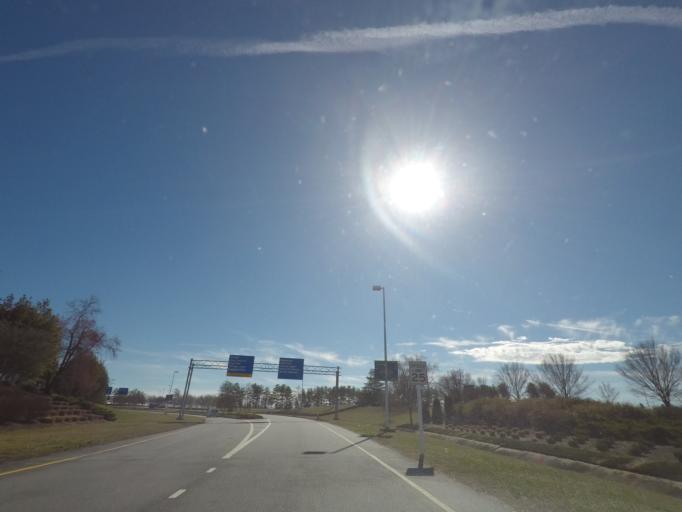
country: US
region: North Carolina
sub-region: Guilford County
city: Oak Ridge
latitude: 36.1038
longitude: -79.9428
